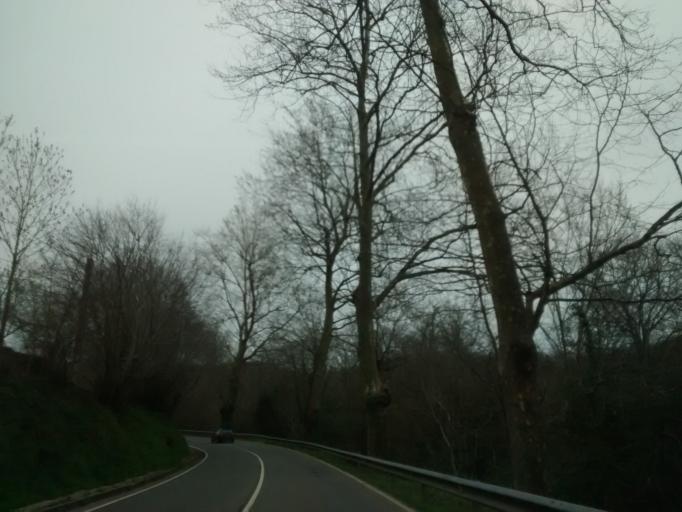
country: ES
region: Cantabria
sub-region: Provincia de Cantabria
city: Lierganes
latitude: 43.3484
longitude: -3.7203
